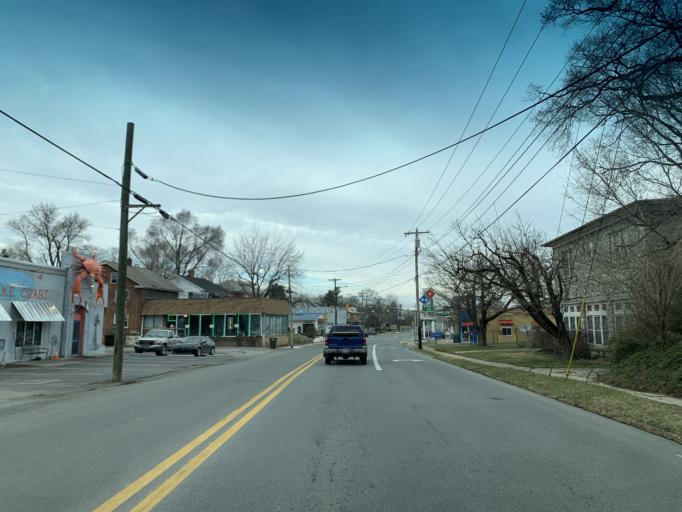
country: US
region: West Virginia
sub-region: Berkeley County
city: Martinsburg
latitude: 39.4468
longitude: -77.9802
